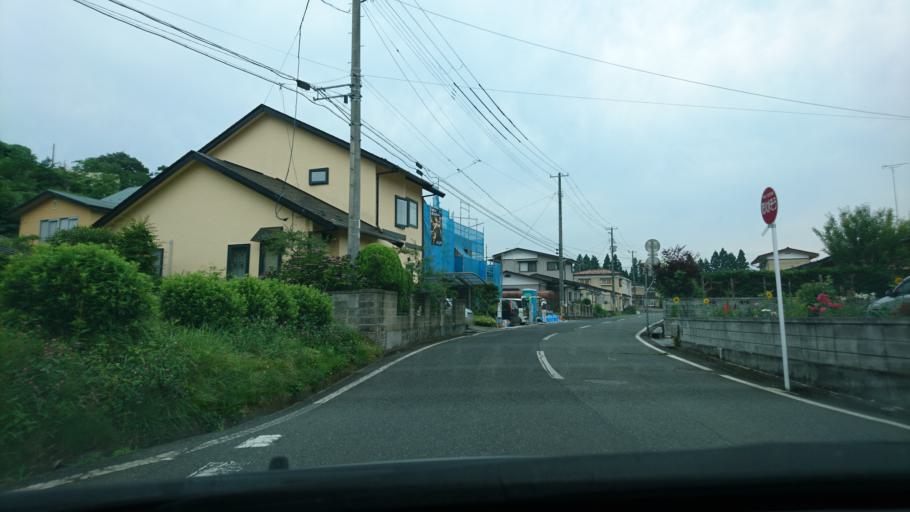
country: JP
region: Iwate
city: Ichinoseki
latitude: 38.9142
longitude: 141.1485
